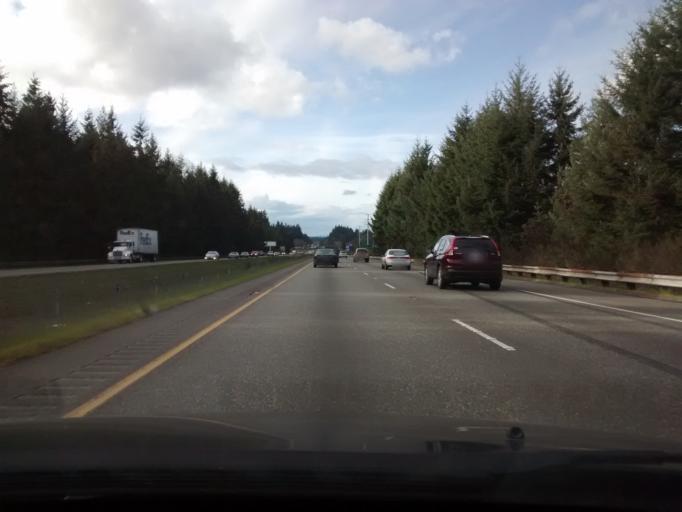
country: US
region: Washington
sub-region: Pierce County
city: Gig Harbor
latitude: 47.3131
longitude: -122.5832
